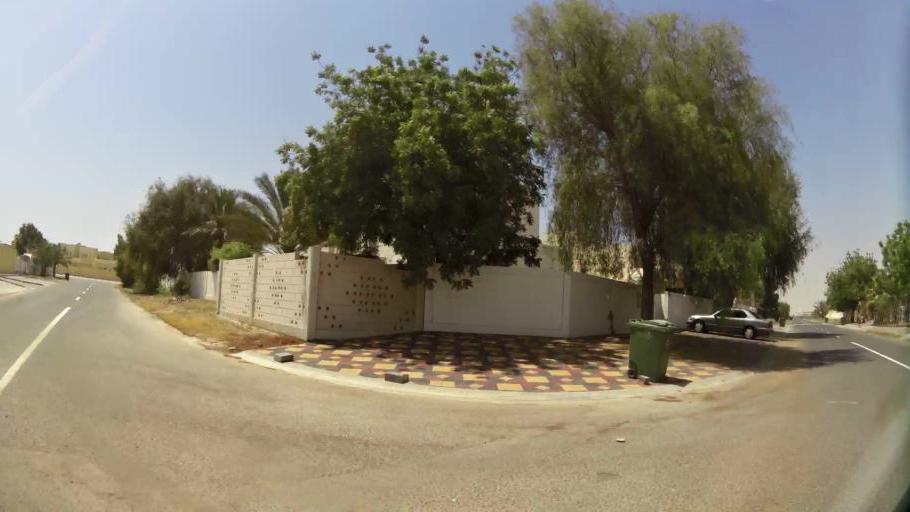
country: AE
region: Ajman
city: Ajman
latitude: 25.4278
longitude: 55.5054
